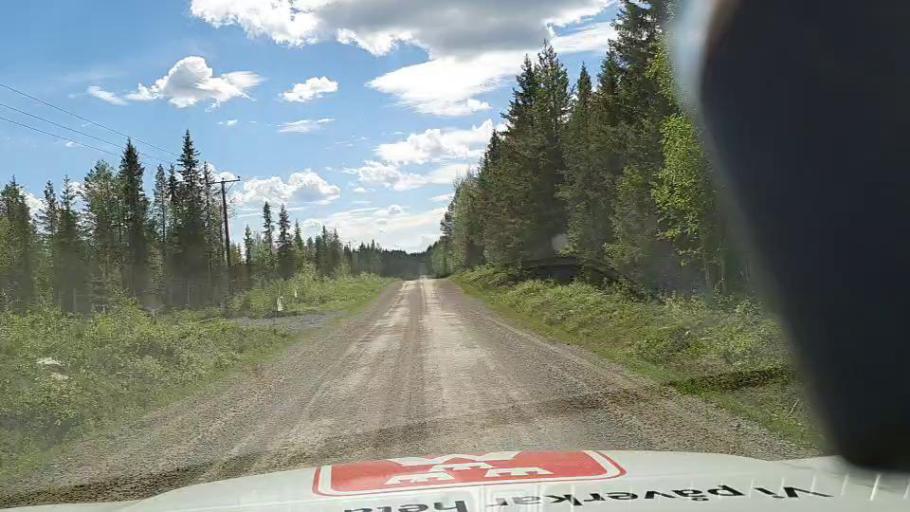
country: SE
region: Jaemtland
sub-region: Stroemsunds Kommun
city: Stroemsund
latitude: 64.5389
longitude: 15.6027
